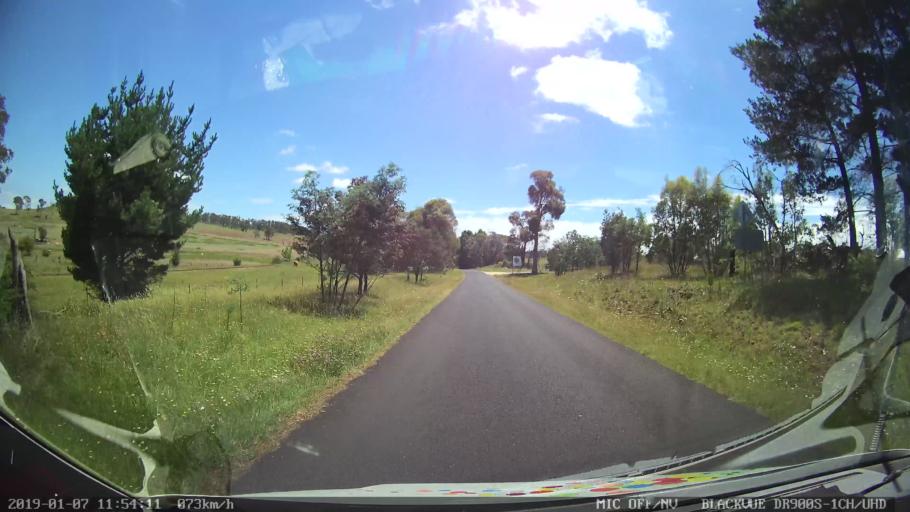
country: AU
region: New South Wales
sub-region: Guyra
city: Guyra
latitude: -30.2989
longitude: 151.6640
